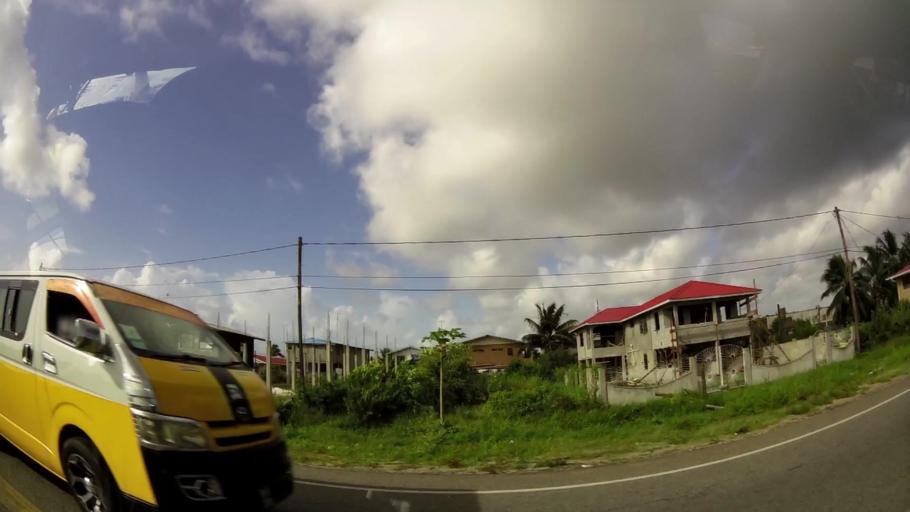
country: GY
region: Demerara-Mahaica
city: Mahaica Village
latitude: 6.7806
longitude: -58.0064
